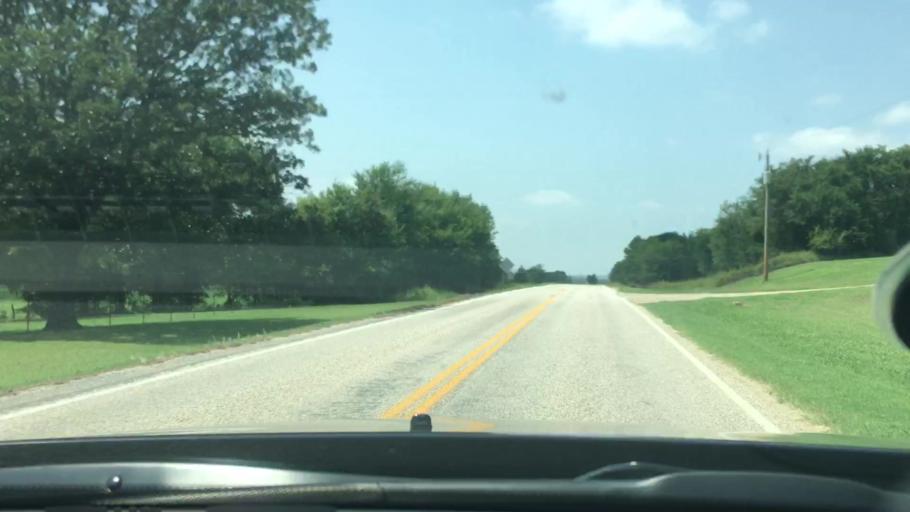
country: US
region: Oklahoma
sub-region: Johnston County
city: Tishomingo
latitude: 34.3731
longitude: -96.4603
